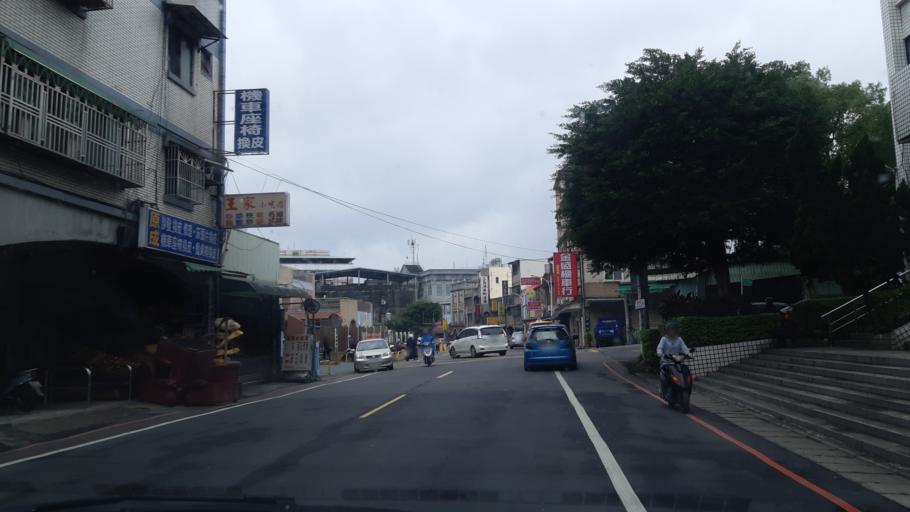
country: TW
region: Taiwan
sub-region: Taoyuan
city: Taoyuan
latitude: 24.9350
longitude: 121.3670
